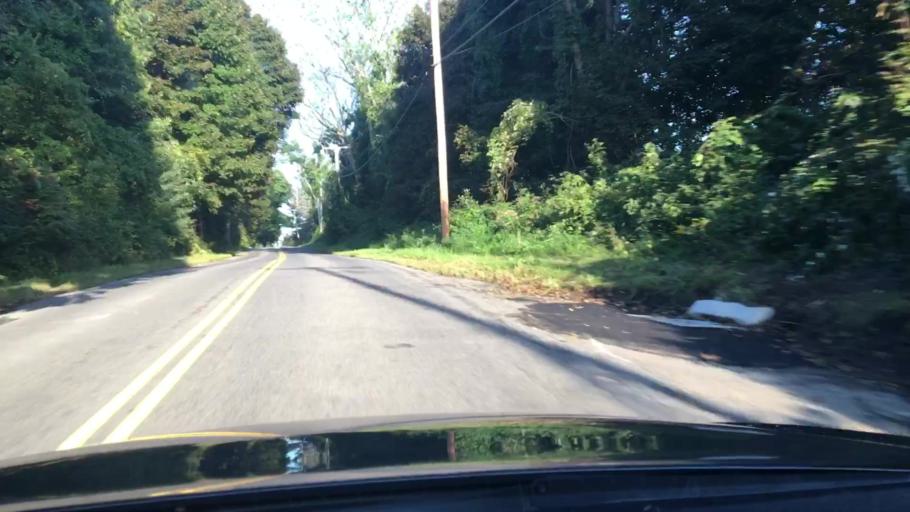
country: US
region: Connecticut
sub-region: Litchfield County
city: New Milford
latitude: 41.6097
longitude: -73.3764
